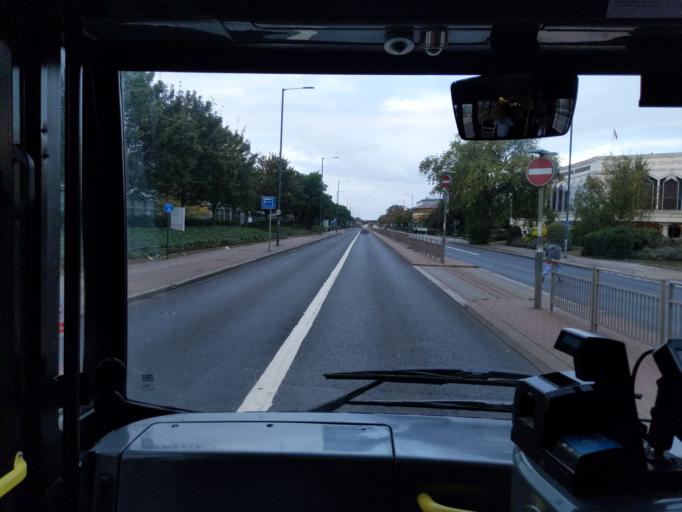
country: GB
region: England
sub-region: Greater London
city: West Drayton
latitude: 51.4808
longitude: -0.4397
